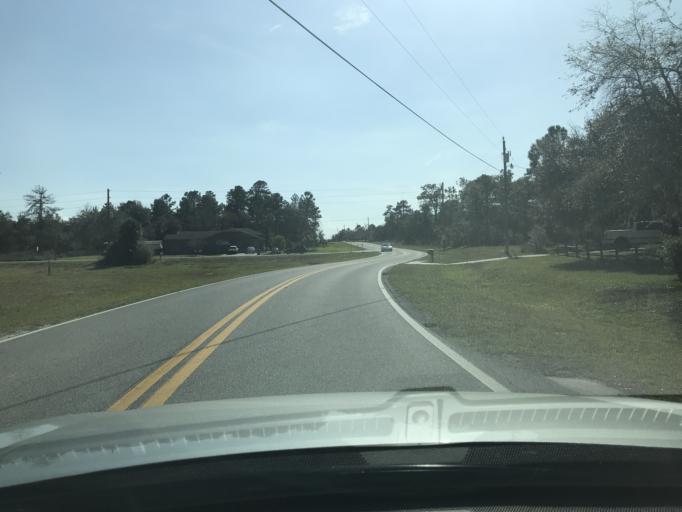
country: US
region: Florida
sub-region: Hernando County
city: North Weeki Wachee
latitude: 28.5388
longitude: -82.5528
